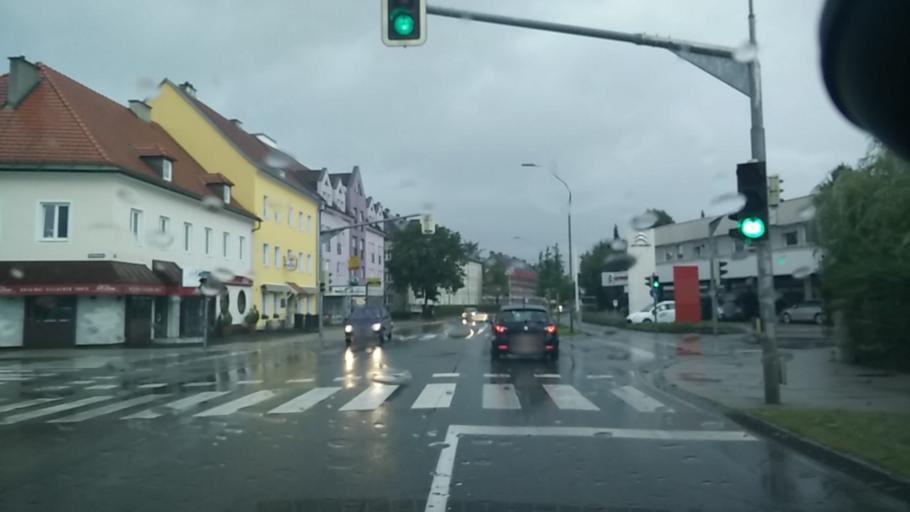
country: AT
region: Carinthia
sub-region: Villach Stadt
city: Villach
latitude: 46.6176
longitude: 13.8603
